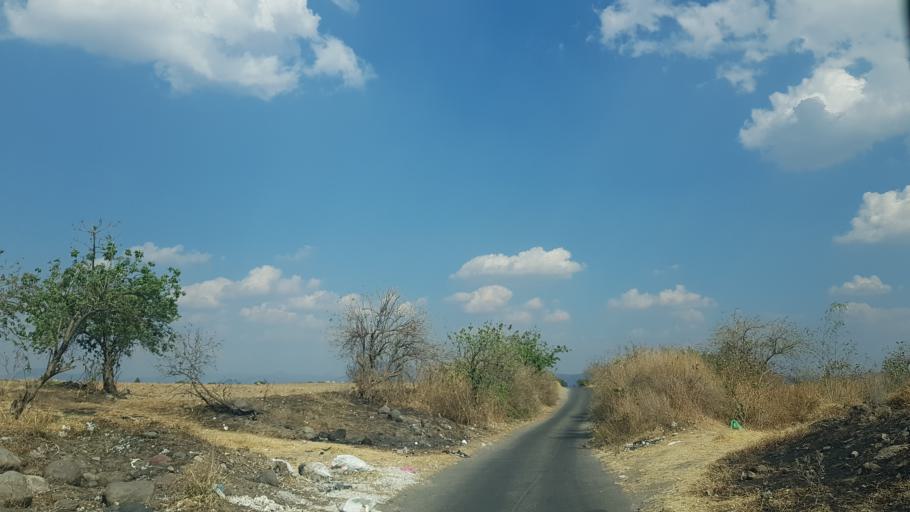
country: MX
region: Puebla
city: Atlixco
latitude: 18.8859
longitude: -98.4961
